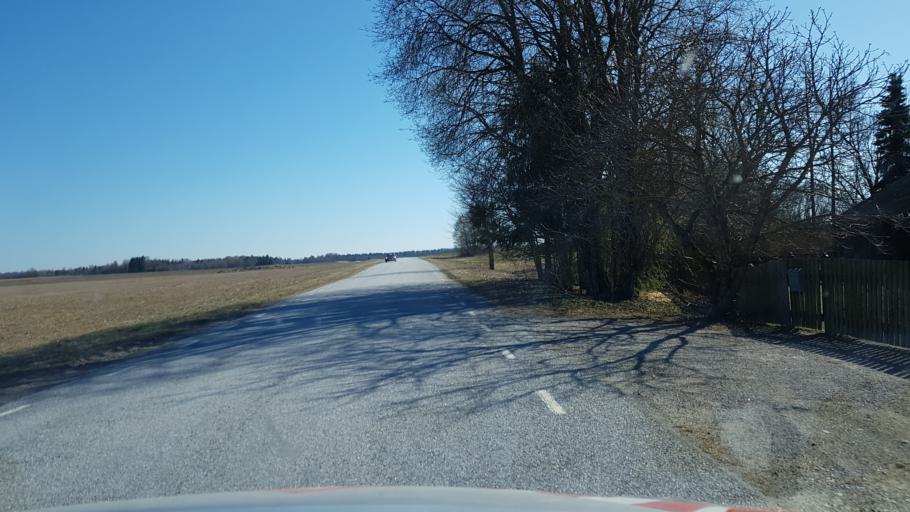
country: EE
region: Jaervamaa
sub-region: Koeru vald
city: Koeru
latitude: 59.0156
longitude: 26.0882
